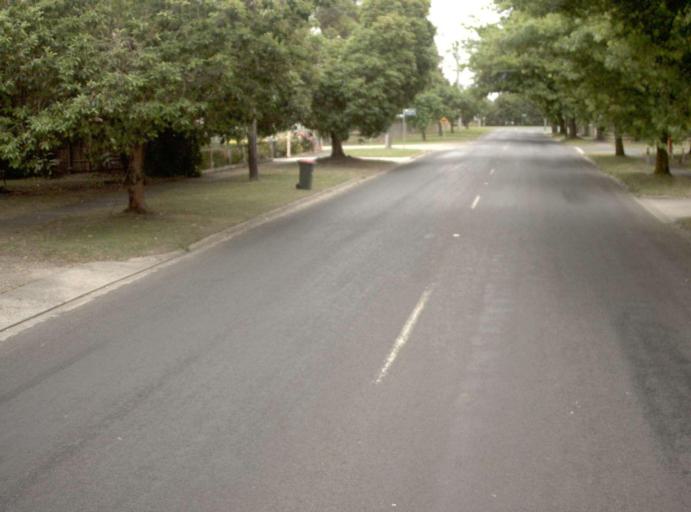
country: AU
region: Victoria
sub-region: Cardinia
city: Bunyip
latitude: -38.1107
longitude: 145.7718
